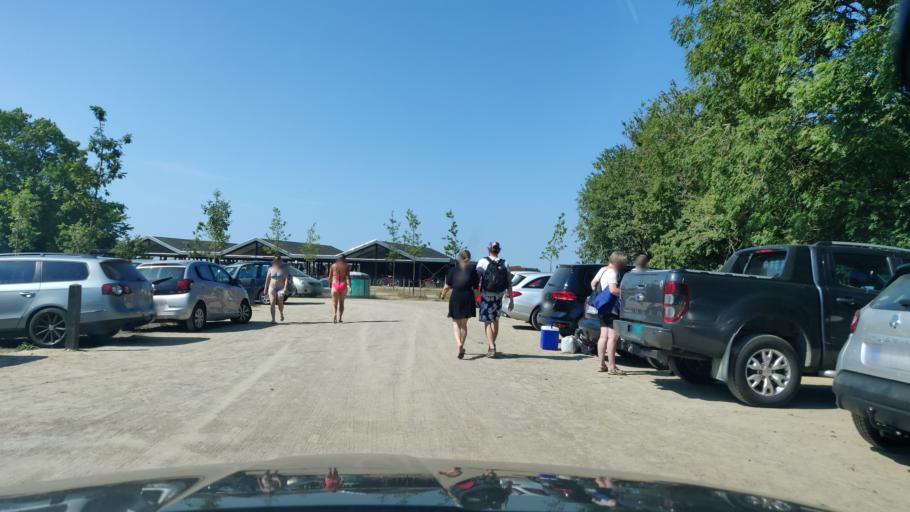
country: DK
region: North Denmark
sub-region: Alborg Kommune
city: Aalborg
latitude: 57.0560
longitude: 9.8875
